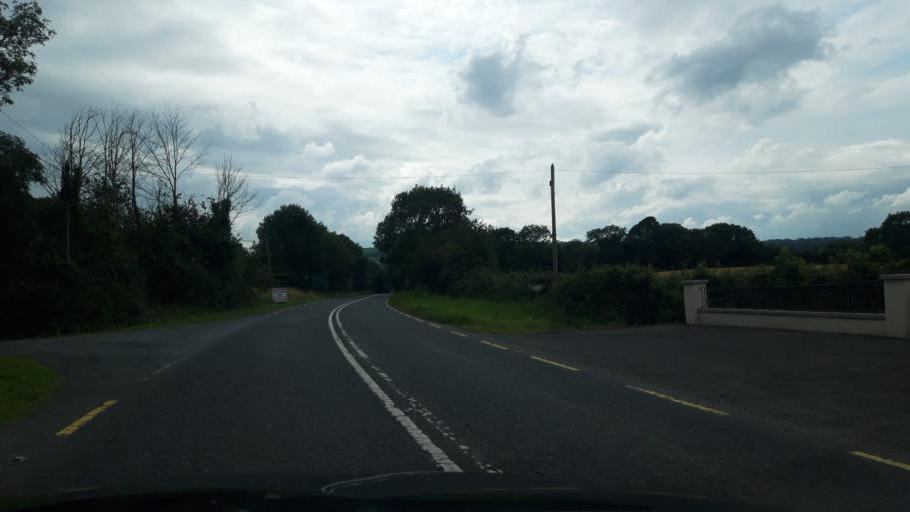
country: IE
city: Ballylinan
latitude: 52.9312
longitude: -7.0560
